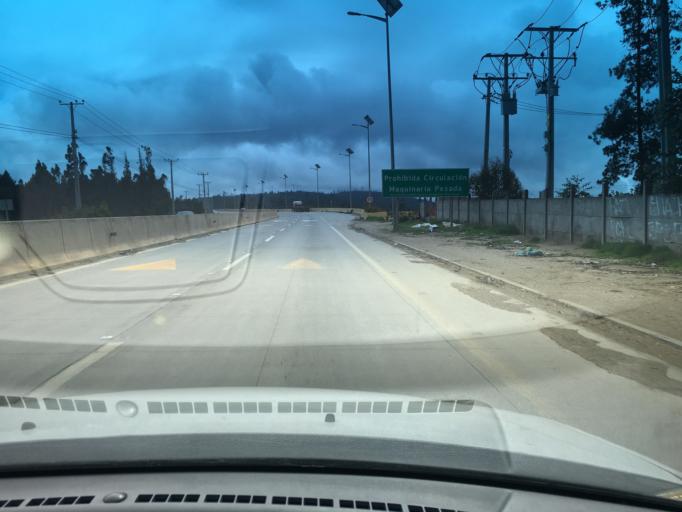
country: CL
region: Valparaiso
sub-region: Provincia de Valparaiso
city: Valparaiso
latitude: -33.0949
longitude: -71.5899
